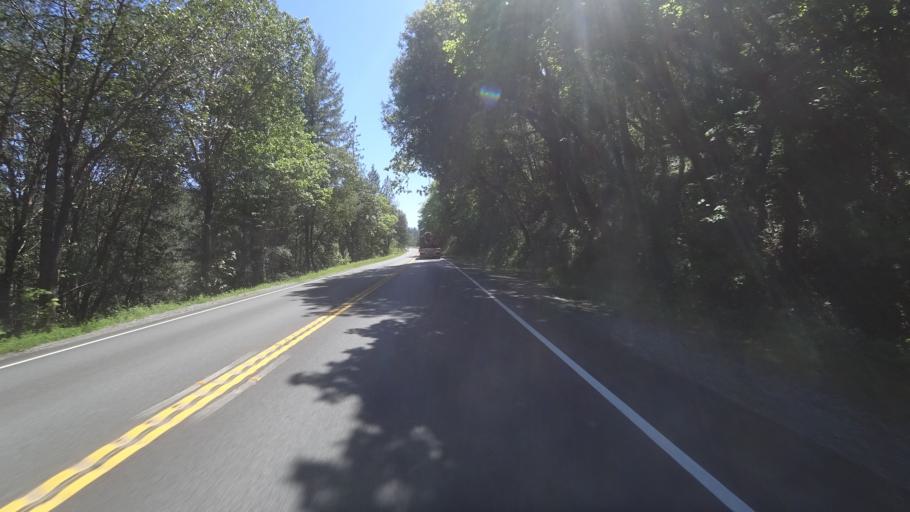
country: US
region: California
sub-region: Humboldt County
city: Willow Creek
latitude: 40.8917
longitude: -123.6075
